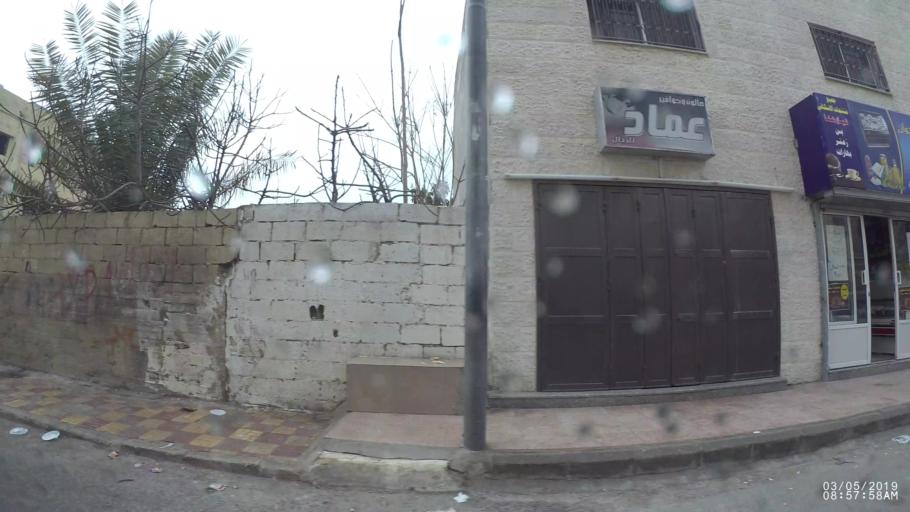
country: JO
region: Amman
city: Amman
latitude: 31.9579
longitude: 35.9391
